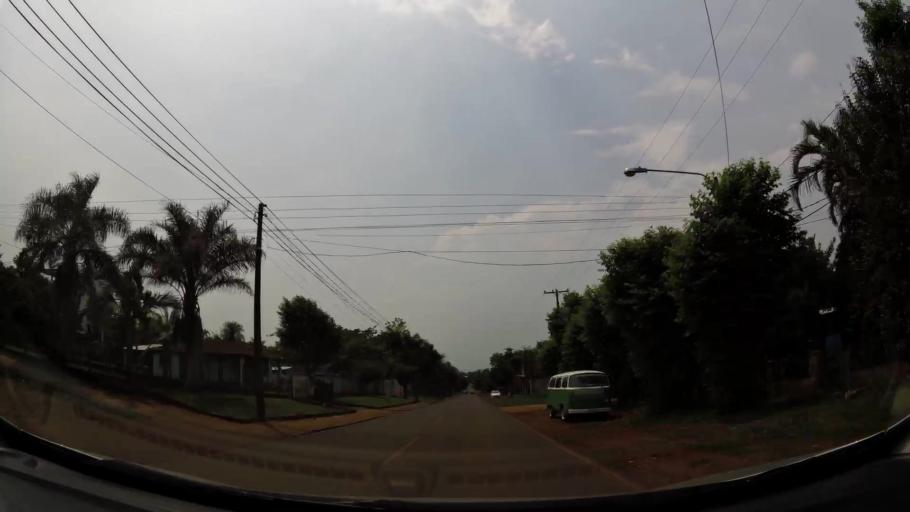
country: BR
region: Parana
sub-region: Foz Do Iguacu
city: Foz do Iguacu
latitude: -25.5715
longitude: -54.6032
